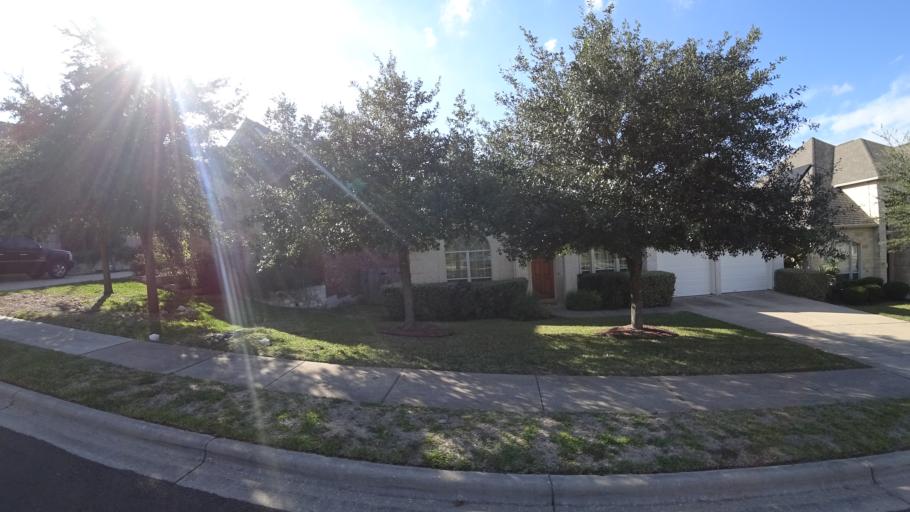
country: US
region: Texas
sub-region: Travis County
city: Barton Creek
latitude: 30.2501
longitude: -97.8753
